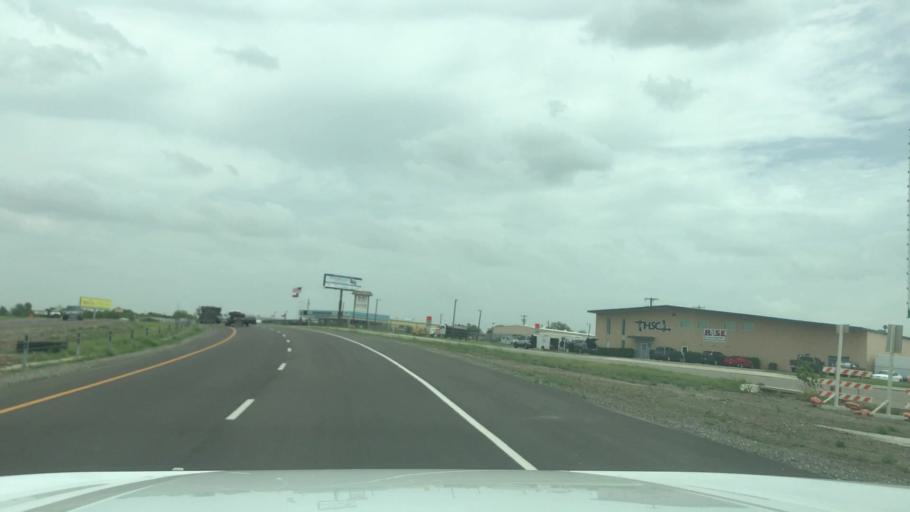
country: US
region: Texas
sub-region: McLennan County
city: Beverly Hills
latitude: 31.4906
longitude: -97.1447
